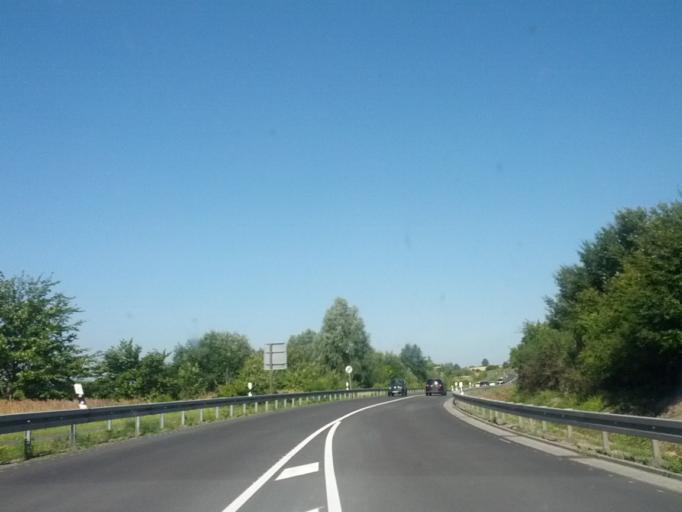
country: DE
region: Mecklenburg-Vorpommern
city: Sagard
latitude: 54.4974
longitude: 13.5647
